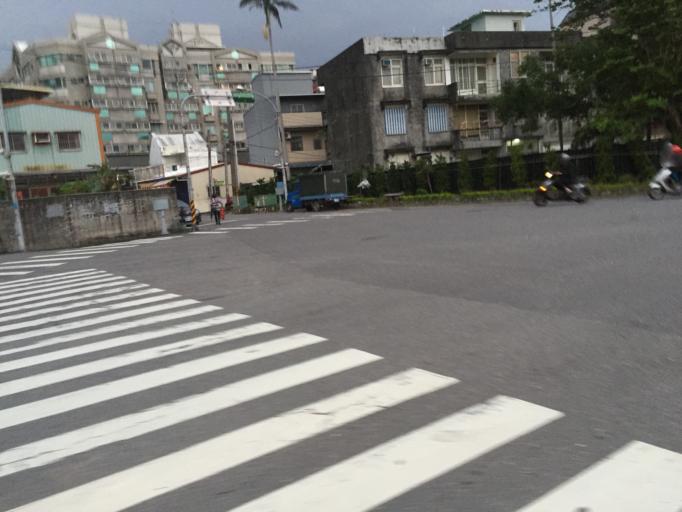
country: TW
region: Taiwan
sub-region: Yilan
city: Yilan
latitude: 24.7540
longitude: 121.7491
